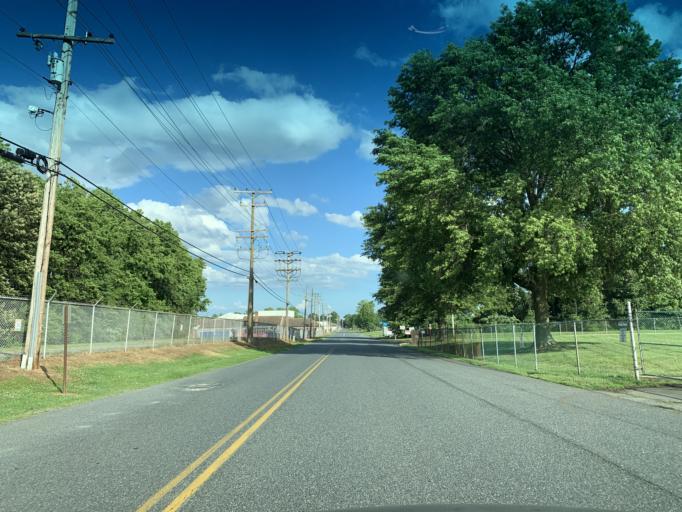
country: US
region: Maryland
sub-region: Harford County
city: Havre de Grace
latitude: 39.5344
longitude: -76.1088
